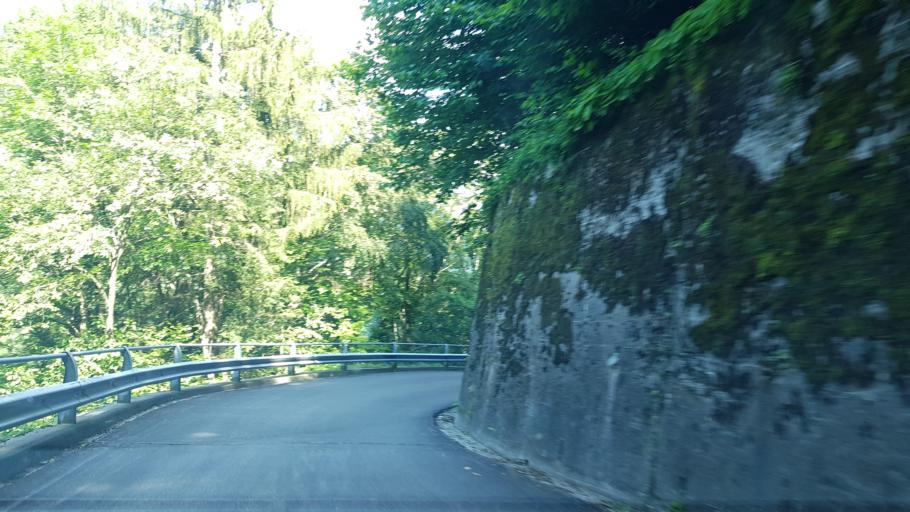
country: IT
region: Friuli Venezia Giulia
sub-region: Provincia di Udine
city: Pontebba
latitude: 46.5136
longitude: 13.2917
